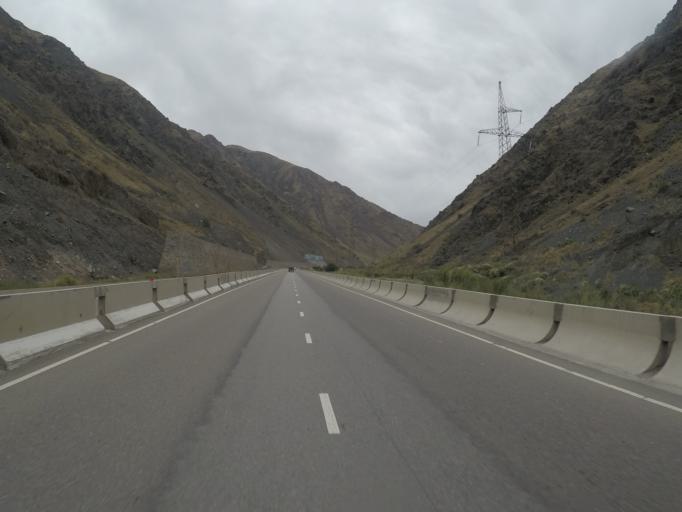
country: KG
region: Chuy
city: Bystrovka
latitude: 42.5694
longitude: 75.8113
